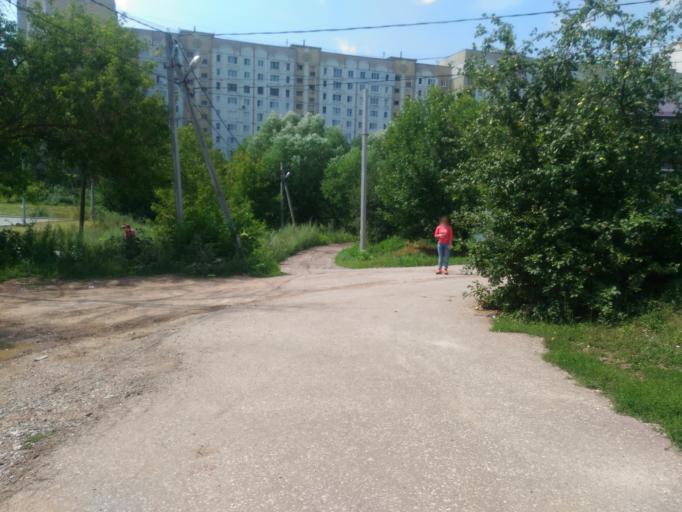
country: RU
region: Tula
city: Mendeleyevskiy
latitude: 54.1604
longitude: 37.6046
